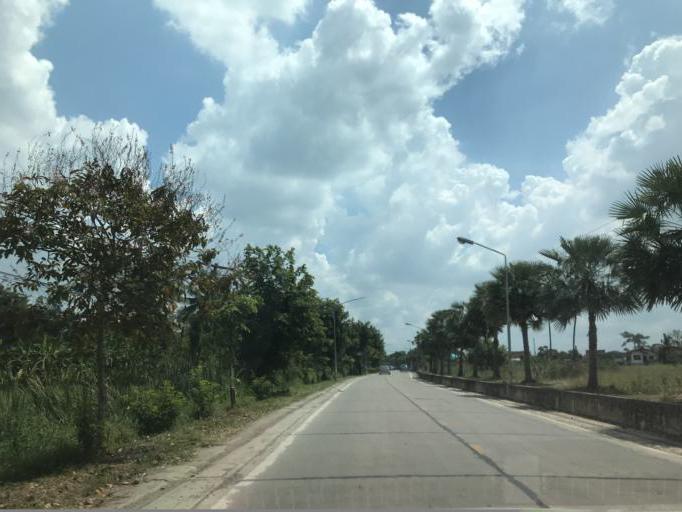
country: TH
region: Pathum Thani
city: Pathum Thani
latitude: 14.0087
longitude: 100.5414
